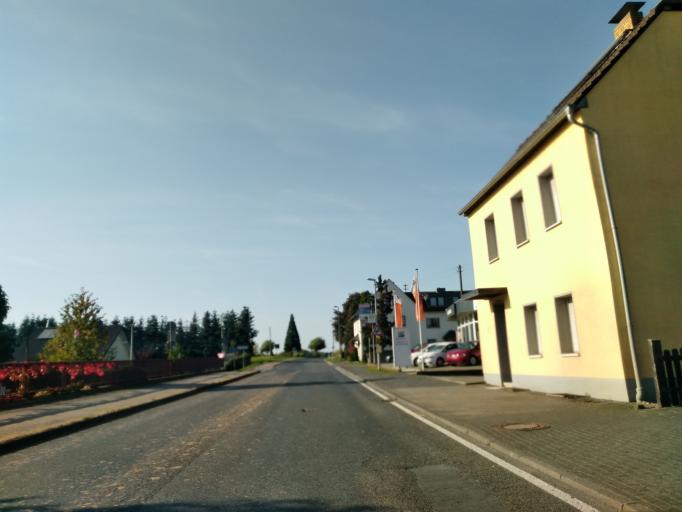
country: DE
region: North Rhine-Westphalia
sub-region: Regierungsbezirk Koln
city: Hennef
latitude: 50.7338
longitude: 7.2592
